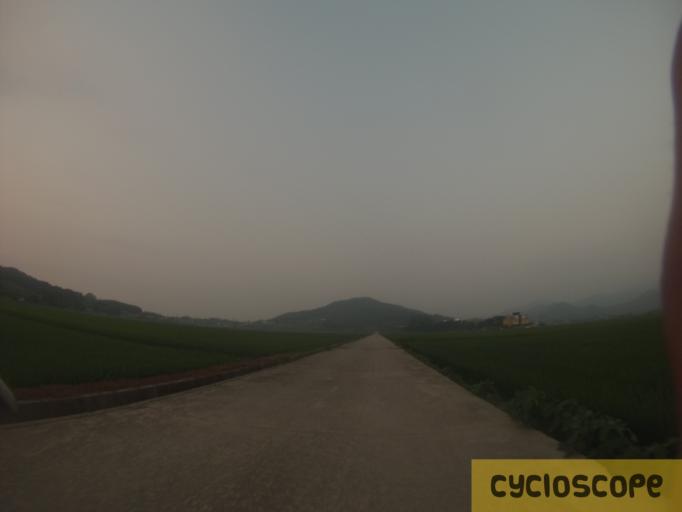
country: KR
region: Jeollabuk-do
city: Puan
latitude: 35.6543
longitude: 126.5012
